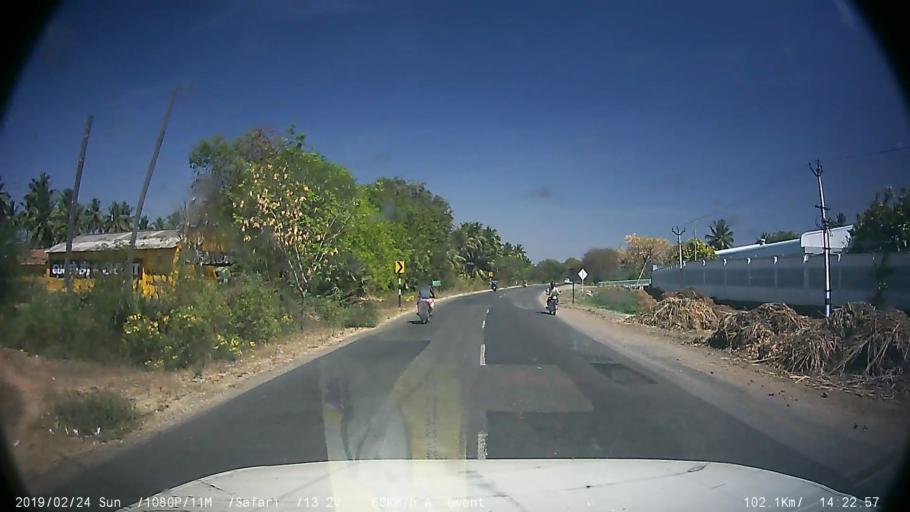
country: IN
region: Tamil Nadu
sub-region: Tiruppur
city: Avinashi
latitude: 11.2021
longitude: 77.2367
